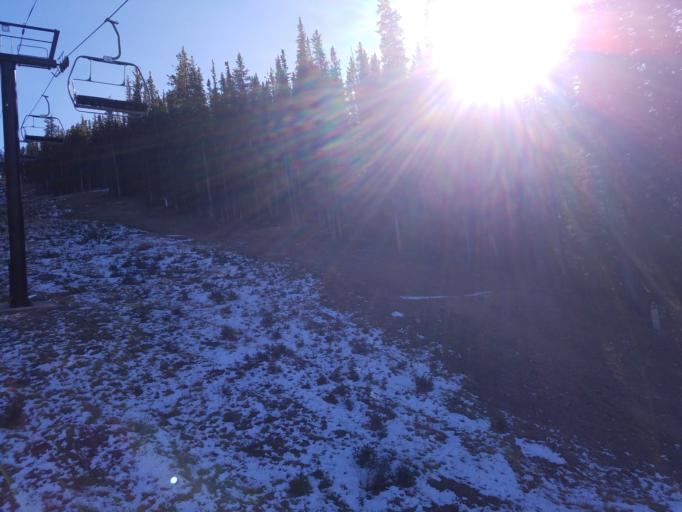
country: US
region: New Mexico
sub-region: Santa Fe County
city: Santa Fe
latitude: 35.7885
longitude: -105.7975
